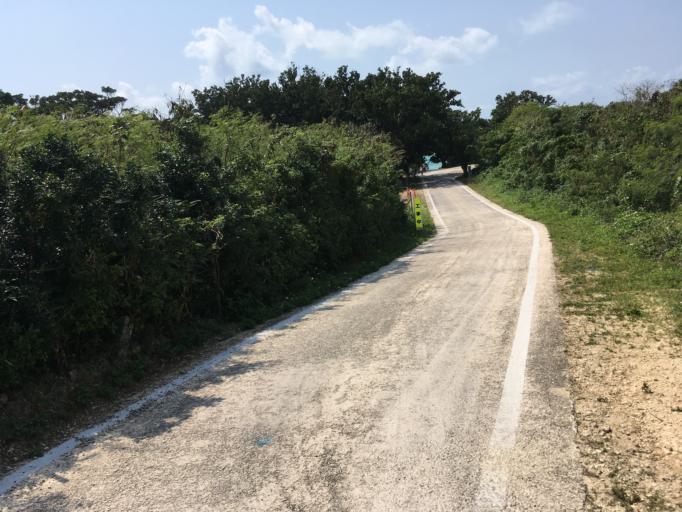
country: JP
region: Okinawa
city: Ishigaki
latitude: 24.3204
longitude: 124.0782
